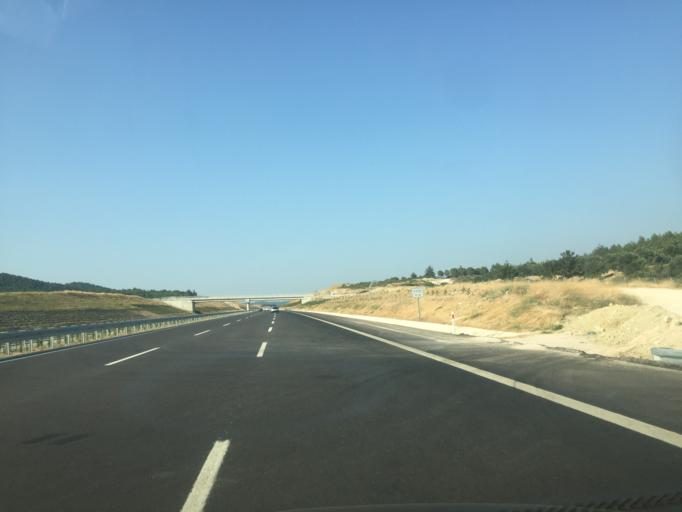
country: TR
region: Manisa
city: Zeytinliova
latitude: 39.0009
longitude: 27.7403
